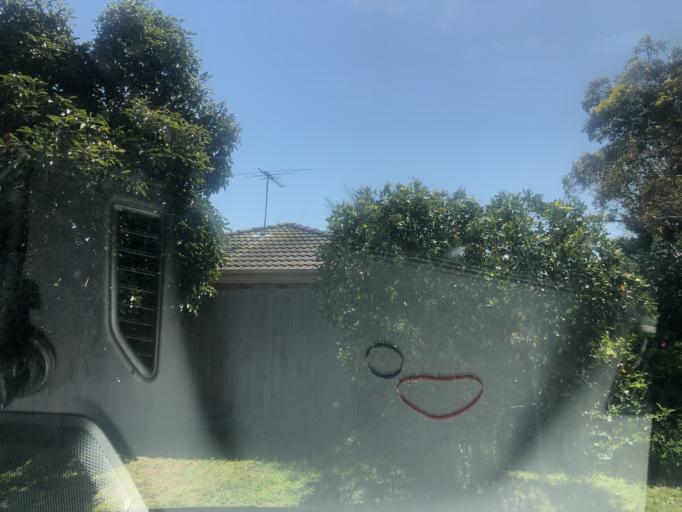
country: AU
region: Victoria
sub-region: Casey
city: Narre Warren South
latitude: -38.0404
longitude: 145.2794
